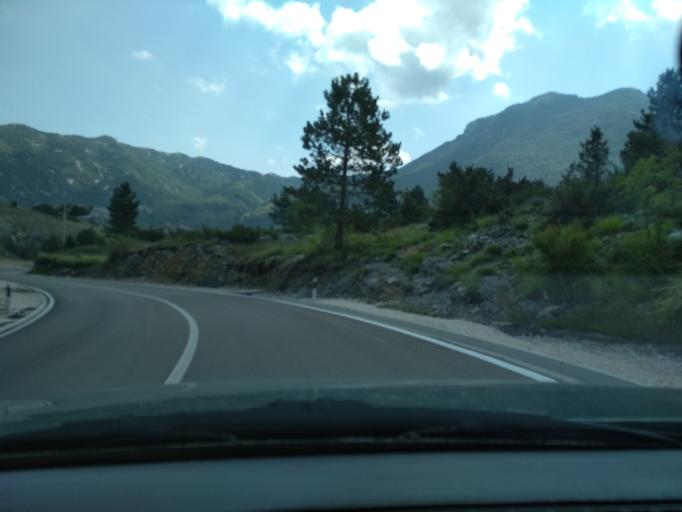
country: ME
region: Kotor
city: Kotor
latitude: 42.4295
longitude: 18.8141
